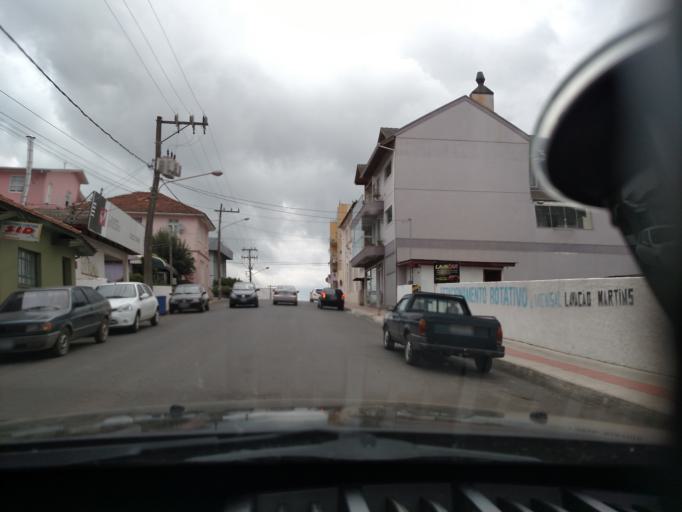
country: BR
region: Santa Catarina
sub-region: Sao Joaquim
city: Sao Joaquim
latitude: -28.2928
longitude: -49.9332
